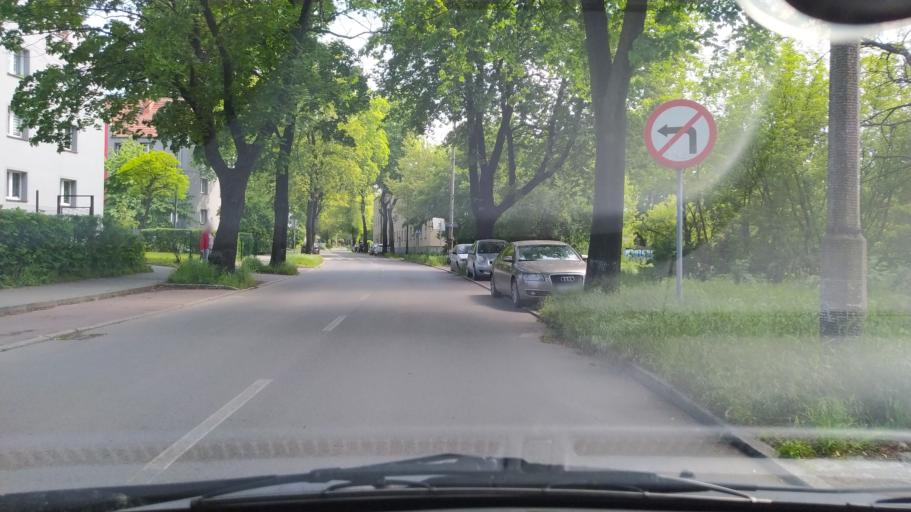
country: PL
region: Silesian Voivodeship
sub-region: Powiat gliwicki
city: Przyszowice
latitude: 50.2899
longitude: 18.7255
